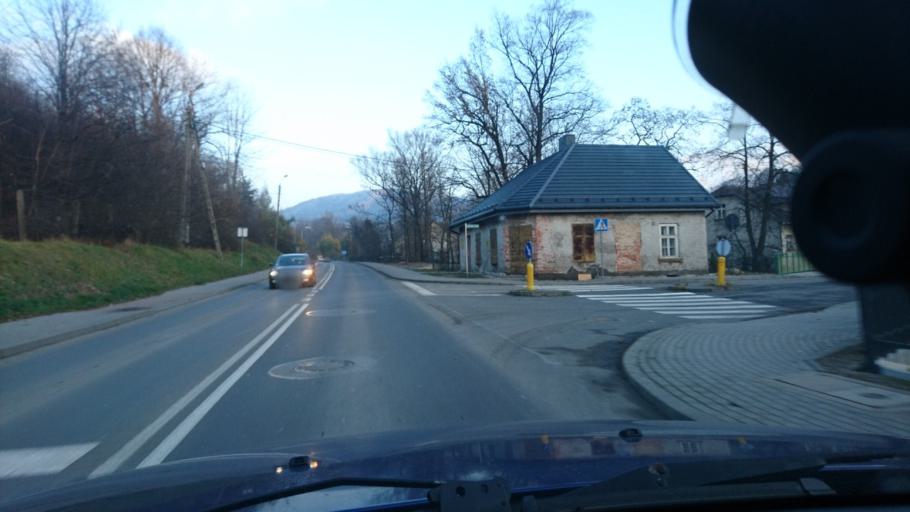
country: PL
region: Silesian Voivodeship
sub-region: Bielsko-Biala
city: Bielsko-Biala
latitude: 49.8155
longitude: 19.0710
